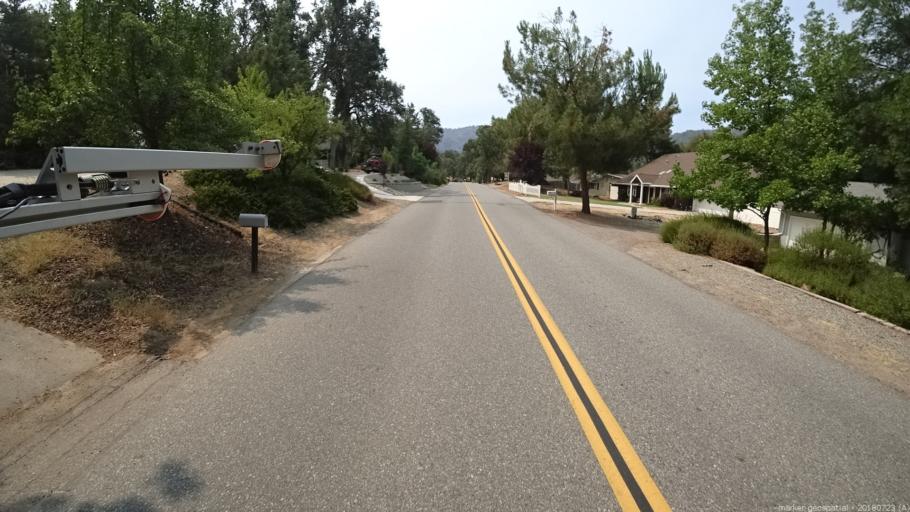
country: US
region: California
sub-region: Madera County
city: Ahwahnee
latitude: 37.3417
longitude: -119.7120
